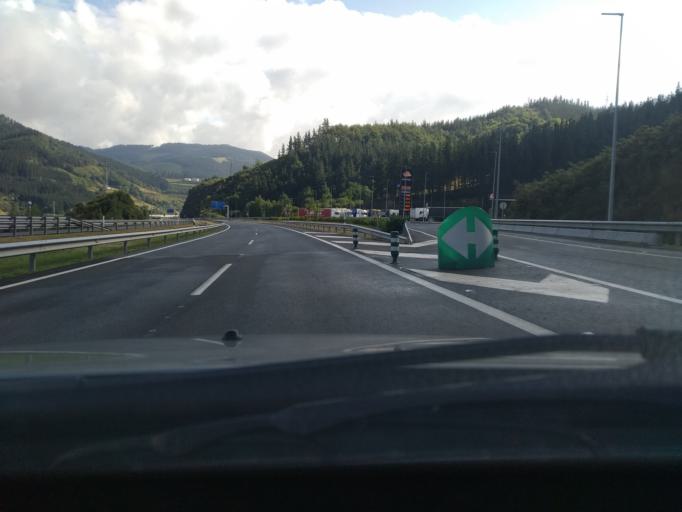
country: ES
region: Basque Country
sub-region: Provincia de Guipuzcoa
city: Arrasate / Mondragon
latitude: 43.0628
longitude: -2.4773
